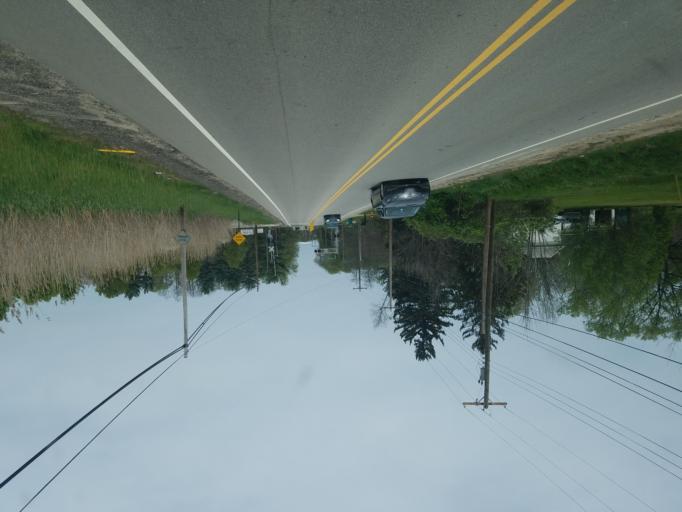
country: US
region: Ohio
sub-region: Summit County
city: Twinsburg
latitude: 41.3215
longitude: -81.4403
